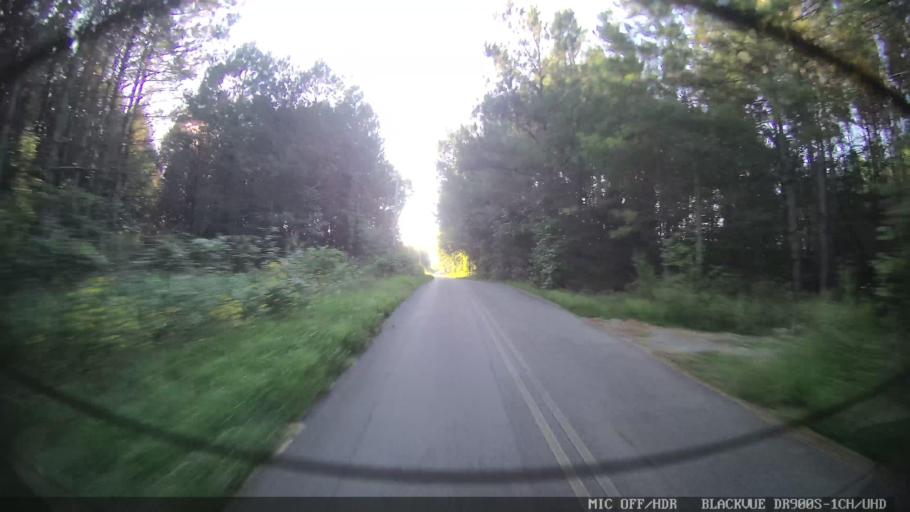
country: US
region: Tennessee
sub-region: Bradley County
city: Wildwood Lake
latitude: 35.0208
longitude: -84.7652
